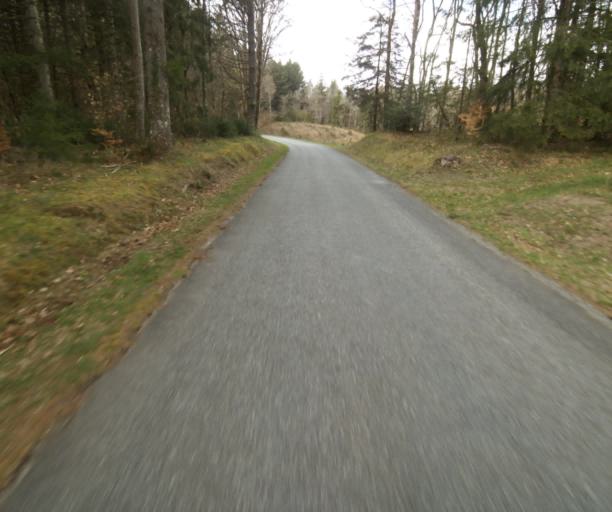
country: FR
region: Limousin
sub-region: Departement de la Correze
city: Correze
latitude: 45.2915
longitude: 1.9642
